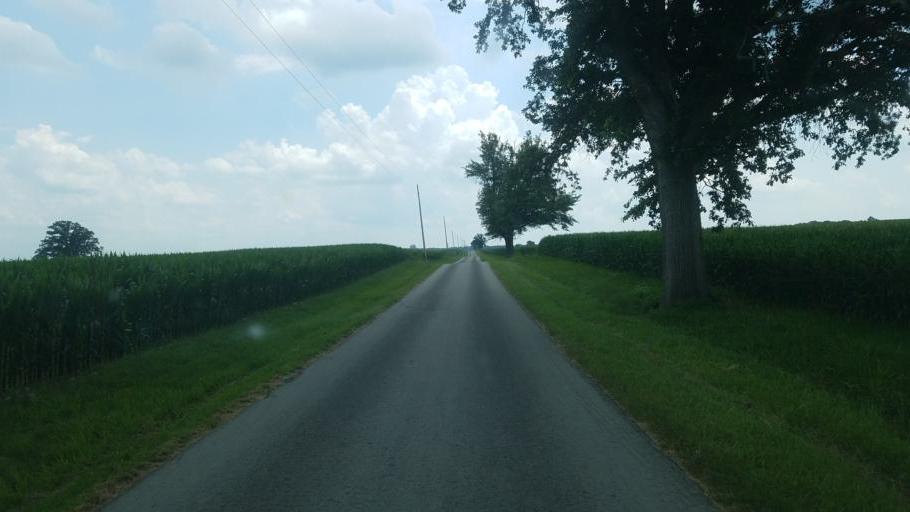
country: US
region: Ohio
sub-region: Hardin County
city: Kenton
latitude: 40.5512
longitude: -83.4850
